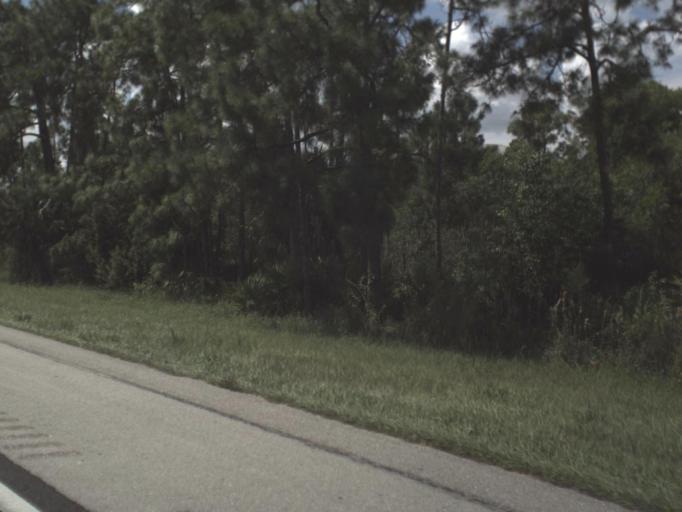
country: US
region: Florida
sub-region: Lee County
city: Three Oaks
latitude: 26.4570
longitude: -81.7867
